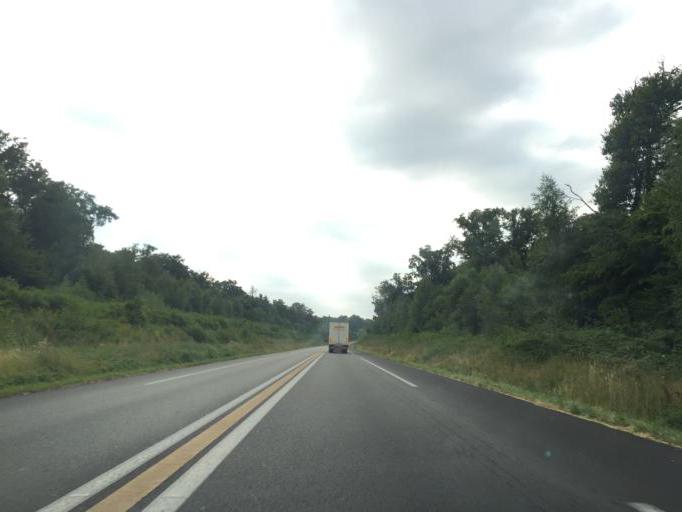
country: FR
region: Auvergne
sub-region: Departement de l'Allier
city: Diou
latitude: 46.5074
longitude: 3.7685
